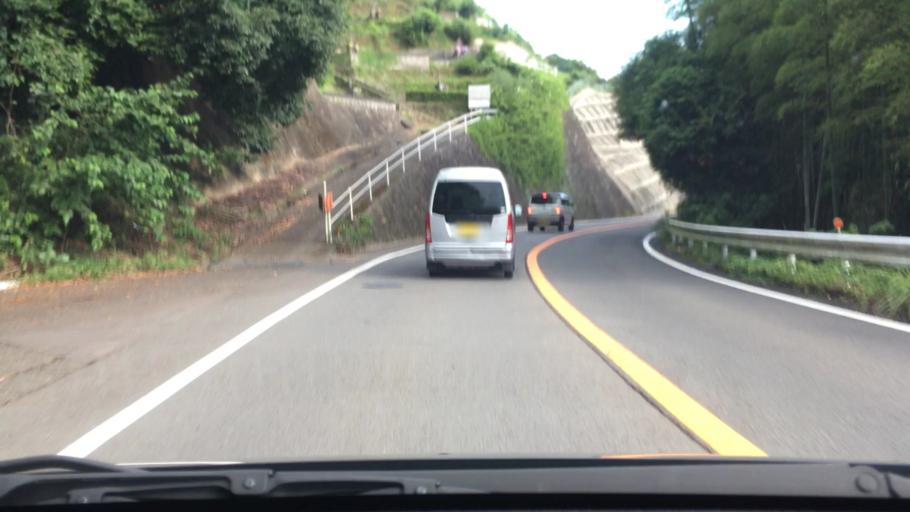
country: JP
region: Nagasaki
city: Togitsu
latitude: 32.8421
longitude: 129.7133
